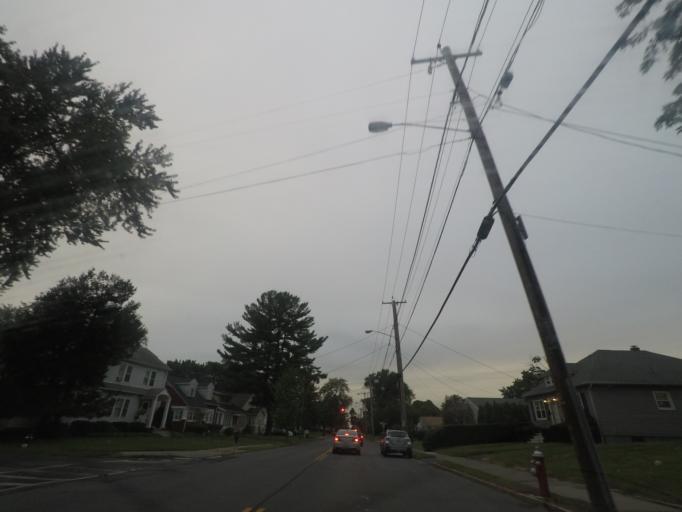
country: US
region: New York
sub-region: Albany County
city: Albany
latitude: 42.6457
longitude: -73.7968
